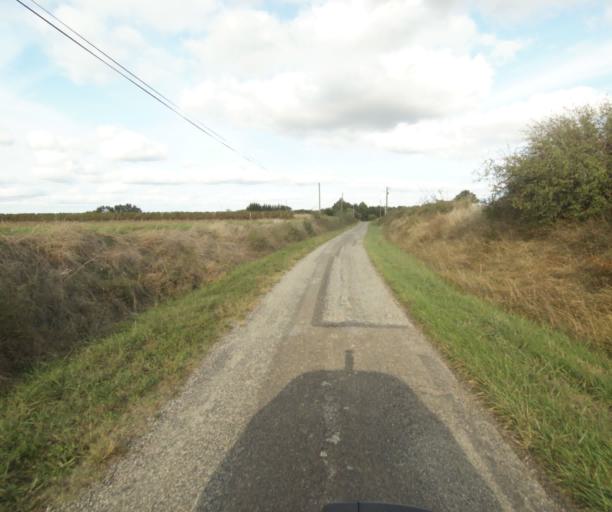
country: FR
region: Midi-Pyrenees
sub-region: Departement de la Haute-Garonne
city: Launac
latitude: 43.8266
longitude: 1.1086
